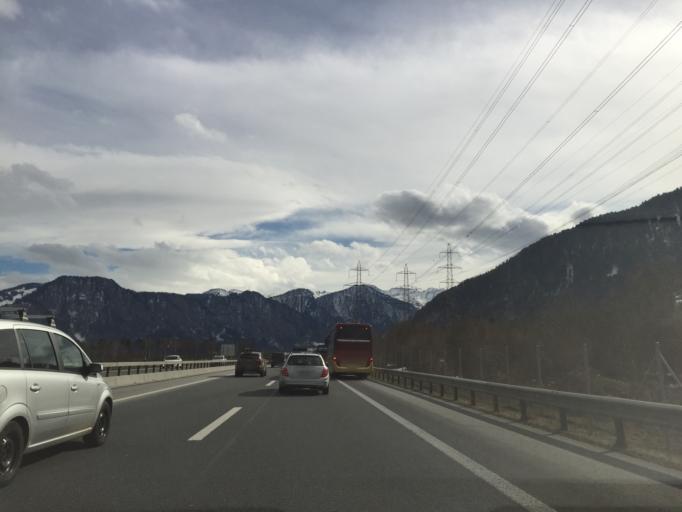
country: CH
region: Grisons
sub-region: Landquart District
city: Maienfeld
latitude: 46.9964
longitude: 9.5262
